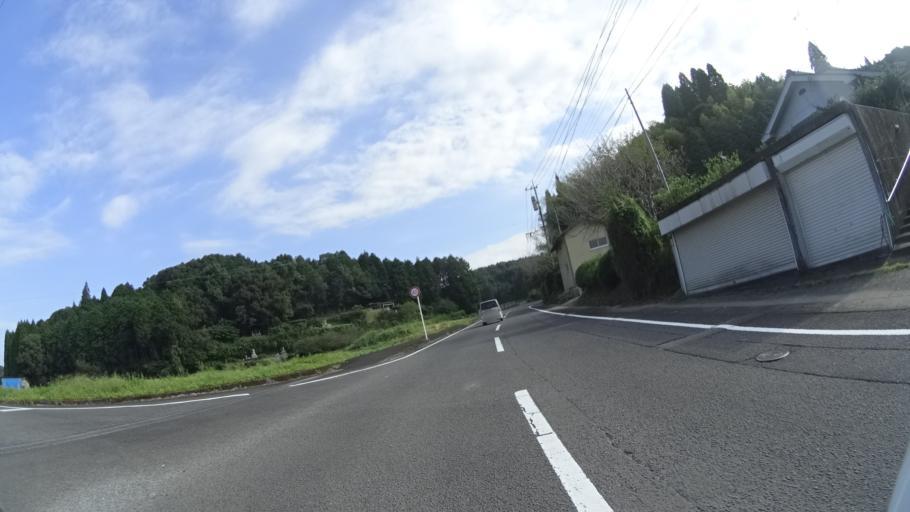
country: JP
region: Kagoshima
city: Okuchi-shinohara
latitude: 32.0137
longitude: 130.6456
